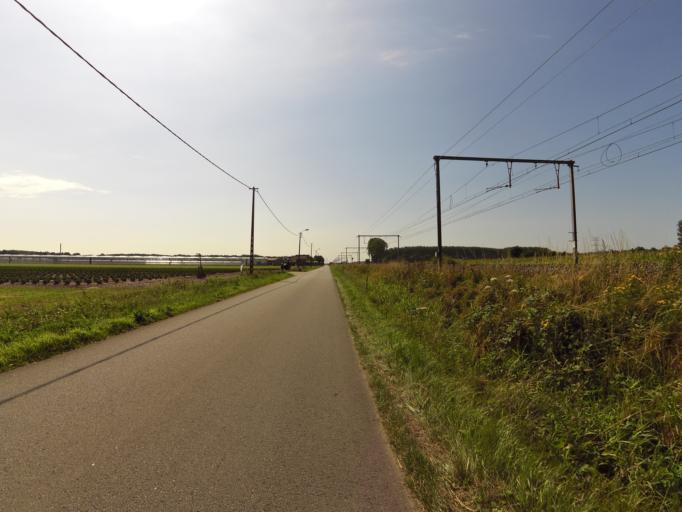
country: BE
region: Flanders
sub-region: Provincie West-Vlaanderen
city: Brugge
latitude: 51.2082
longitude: 3.1697
